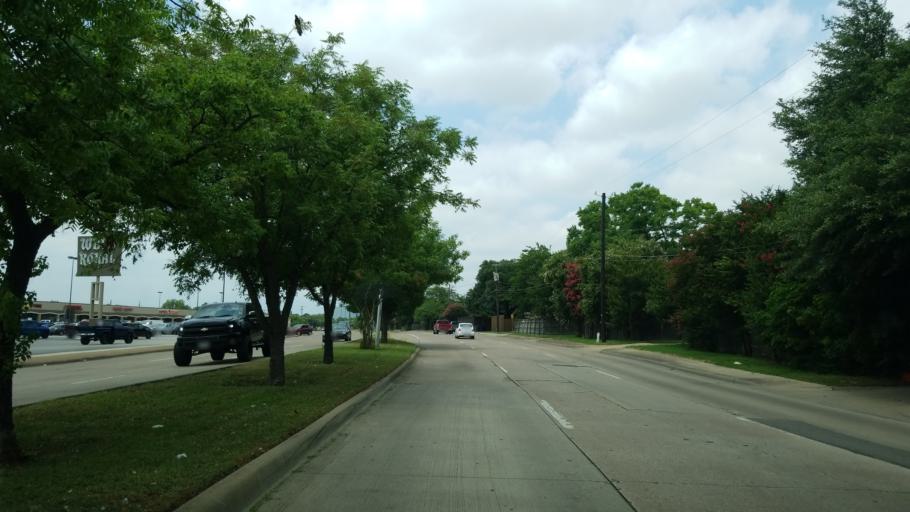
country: US
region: Texas
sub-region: Dallas County
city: Farmers Branch
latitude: 32.8961
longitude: -96.8705
